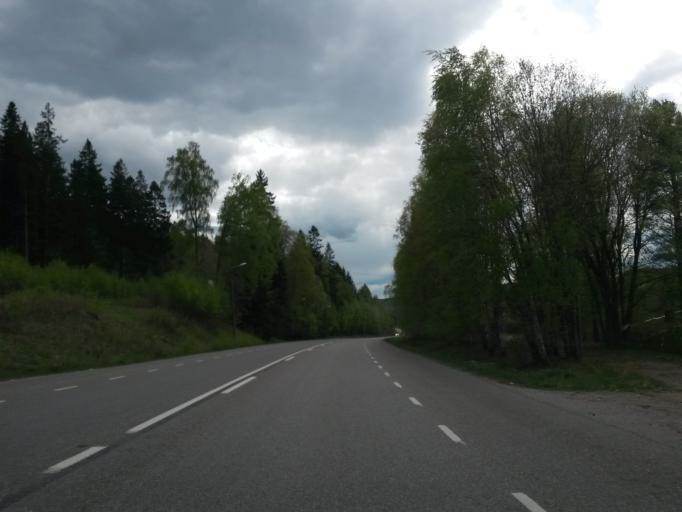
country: SE
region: Vaestra Goetaland
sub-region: Boras Kommun
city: Boras
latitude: 57.7802
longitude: 12.9884
